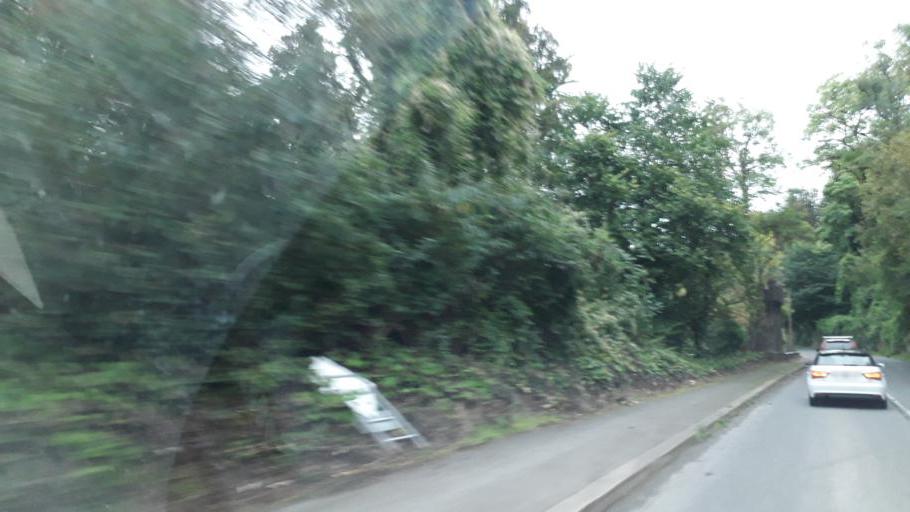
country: IE
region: Leinster
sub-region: Wicklow
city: Enniskerry
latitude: 53.1904
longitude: -6.1542
